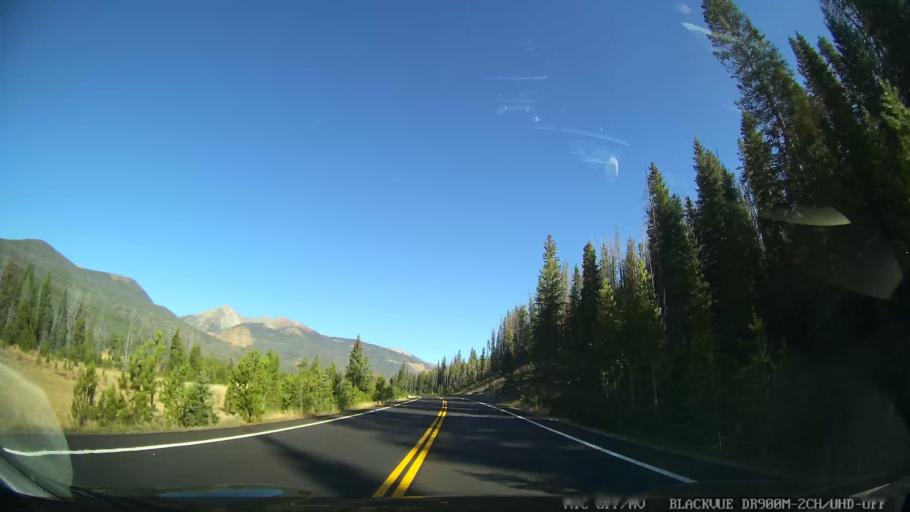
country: US
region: Colorado
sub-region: Grand County
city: Granby
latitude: 40.3320
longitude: -105.8548
